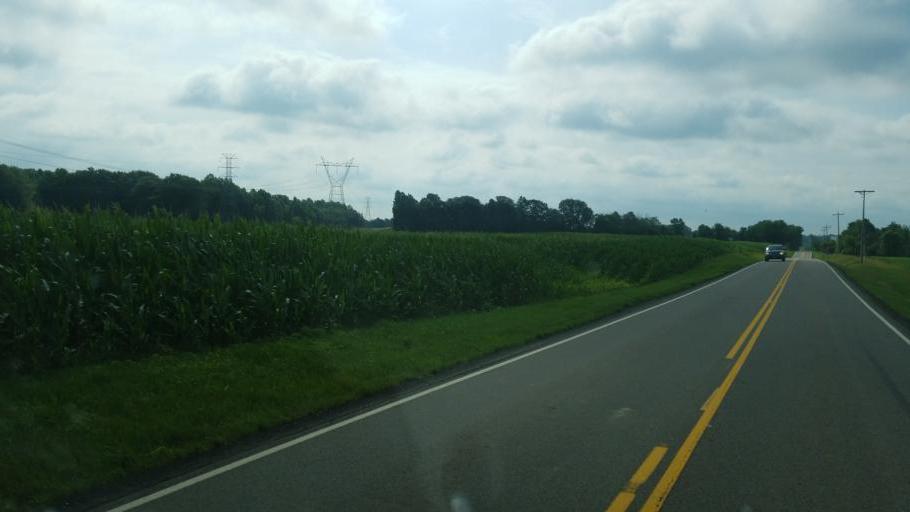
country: US
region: Ohio
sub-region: Knox County
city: Centerburg
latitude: 40.2524
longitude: -82.5901
